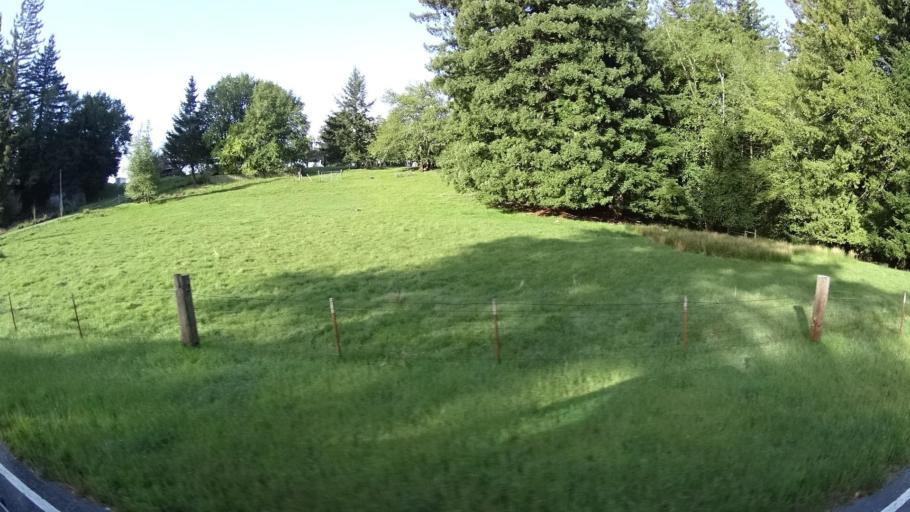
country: US
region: California
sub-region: Humboldt County
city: Bayside
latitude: 40.7578
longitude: -123.9916
